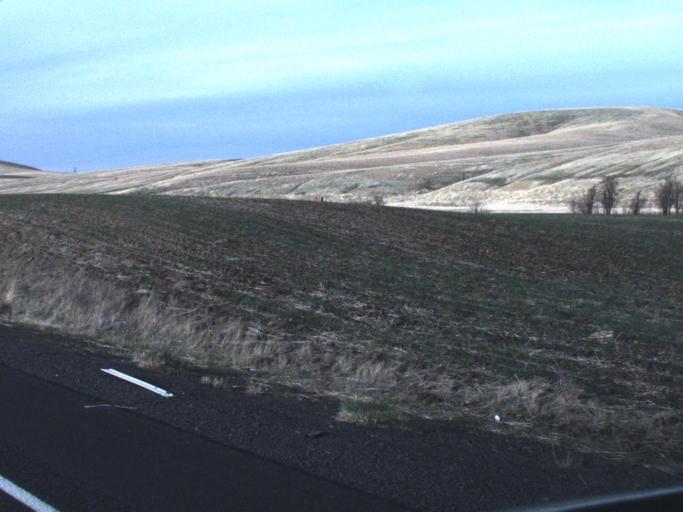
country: US
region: Washington
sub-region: Columbia County
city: Dayton
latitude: 46.5383
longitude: -117.8595
